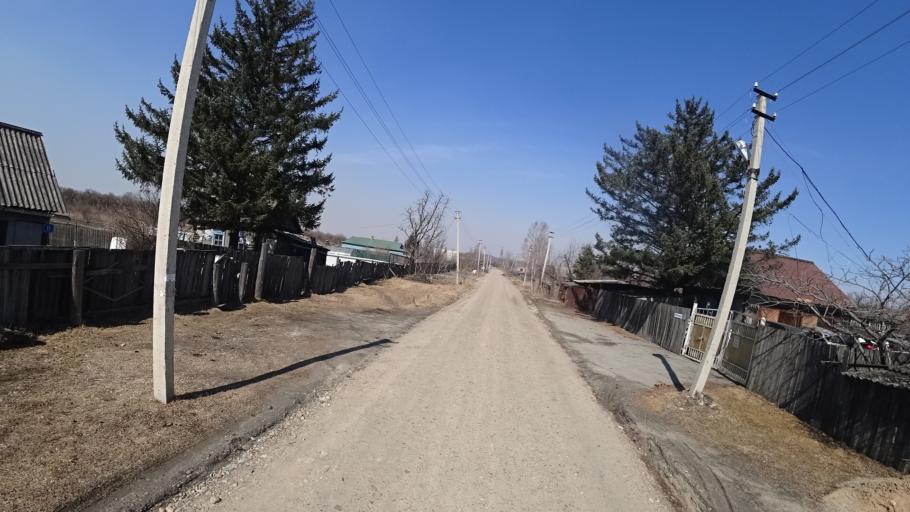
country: RU
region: Amur
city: Novobureyskiy
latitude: 49.7892
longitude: 129.8538
